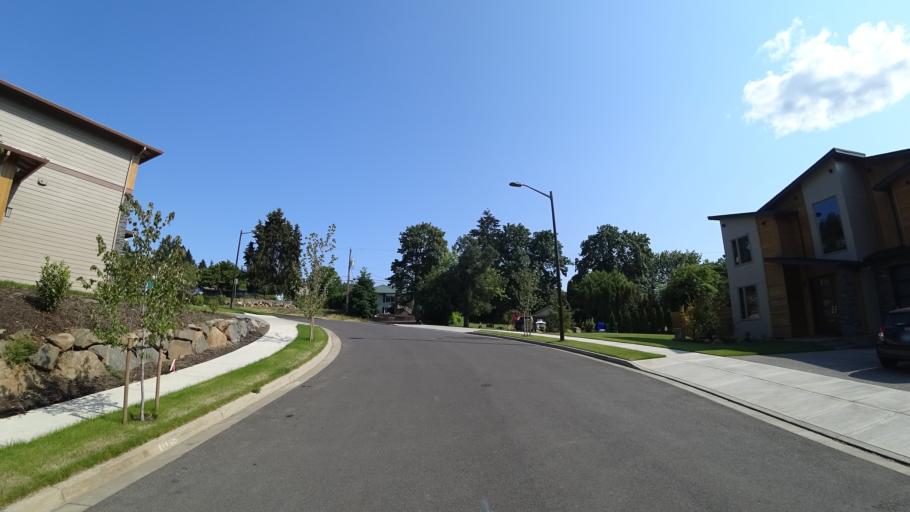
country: US
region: Oregon
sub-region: Clackamas County
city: Happy Valley
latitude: 45.4362
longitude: -122.5370
